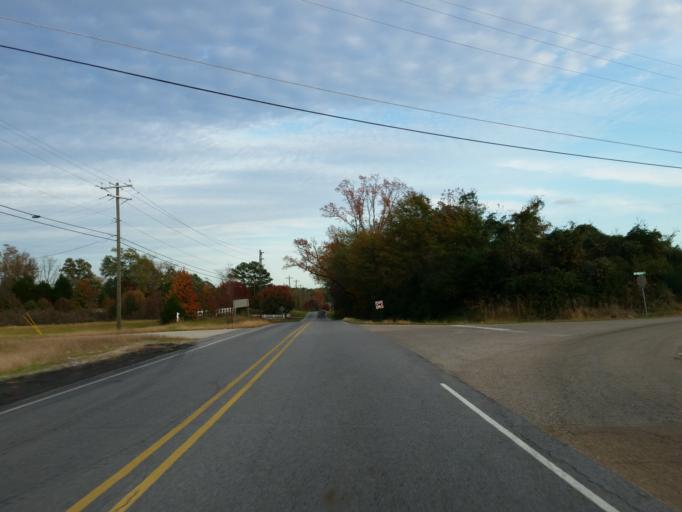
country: US
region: Mississippi
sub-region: Lauderdale County
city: Marion
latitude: 32.4123
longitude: -88.6194
